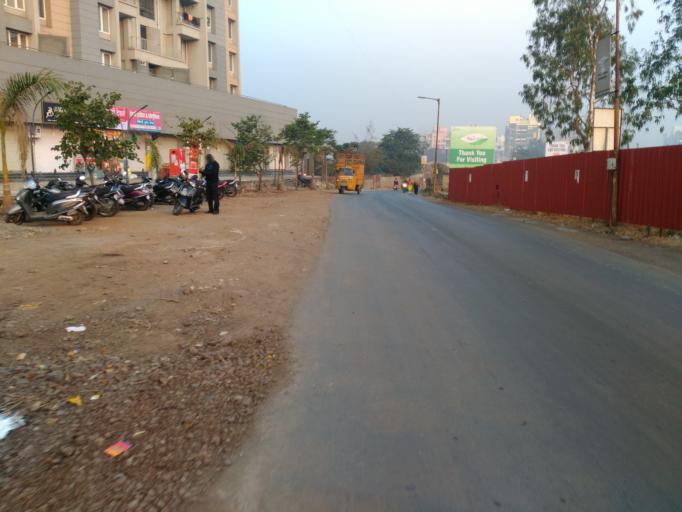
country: IN
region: Maharashtra
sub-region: Pune Division
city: Pune
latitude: 18.4496
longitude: 73.8845
